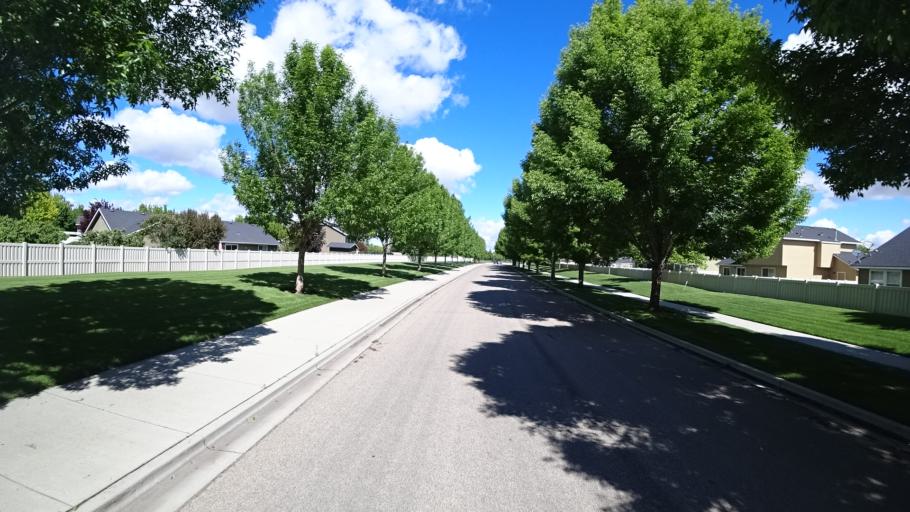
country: US
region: Idaho
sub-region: Ada County
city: Kuna
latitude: 43.5040
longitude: -116.4400
